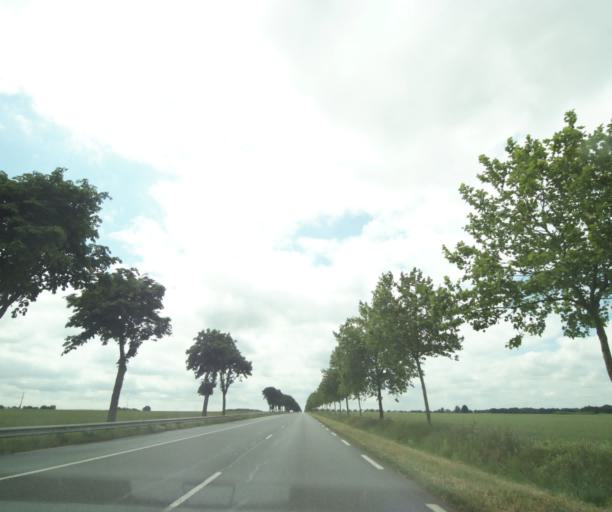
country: FR
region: Poitou-Charentes
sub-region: Departement des Deux-Sevres
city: Saint-Jean-de-Thouars
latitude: 46.9530
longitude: -0.2067
